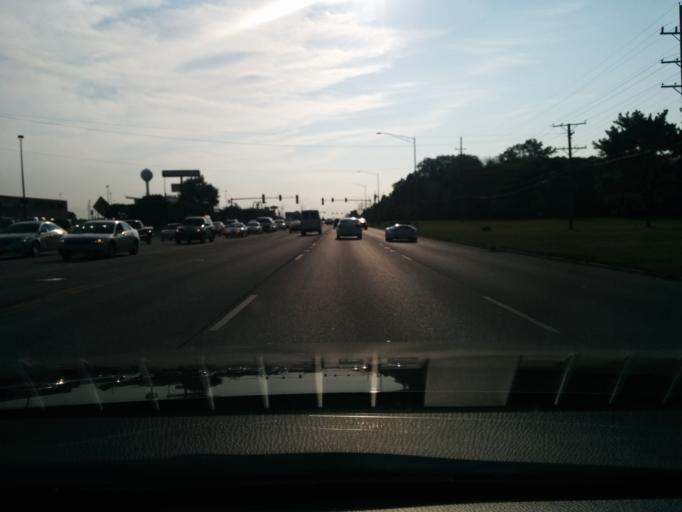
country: US
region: Illinois
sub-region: Cook County
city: River Grove
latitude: 41.9085
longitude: -87.8301
